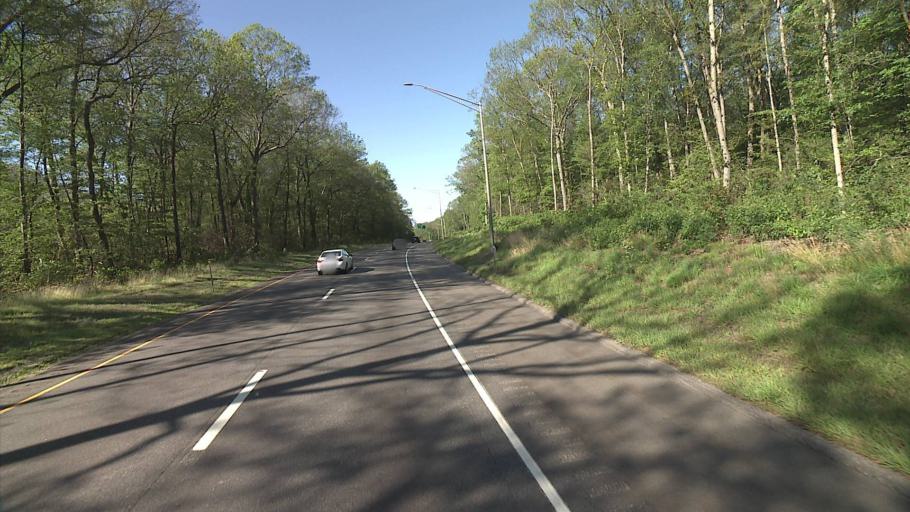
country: US
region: Connecticut
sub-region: New London County
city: Uncasville
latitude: 41.4325
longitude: -72.1214
